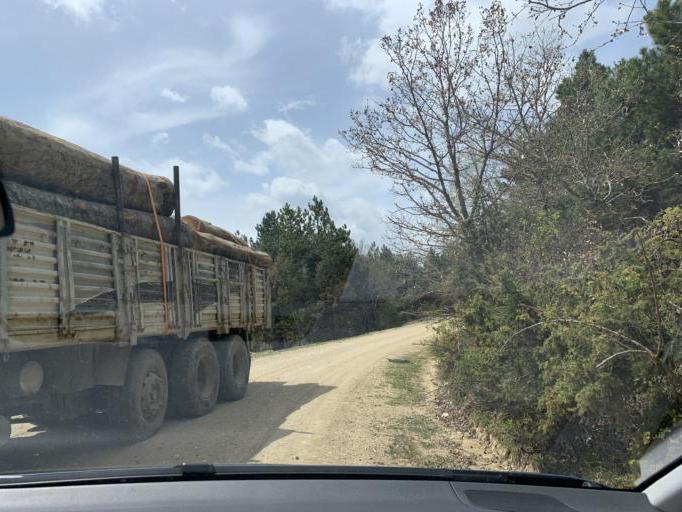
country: TR
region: Bolu
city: Bolu
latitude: 40.8301
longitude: 31.6769
